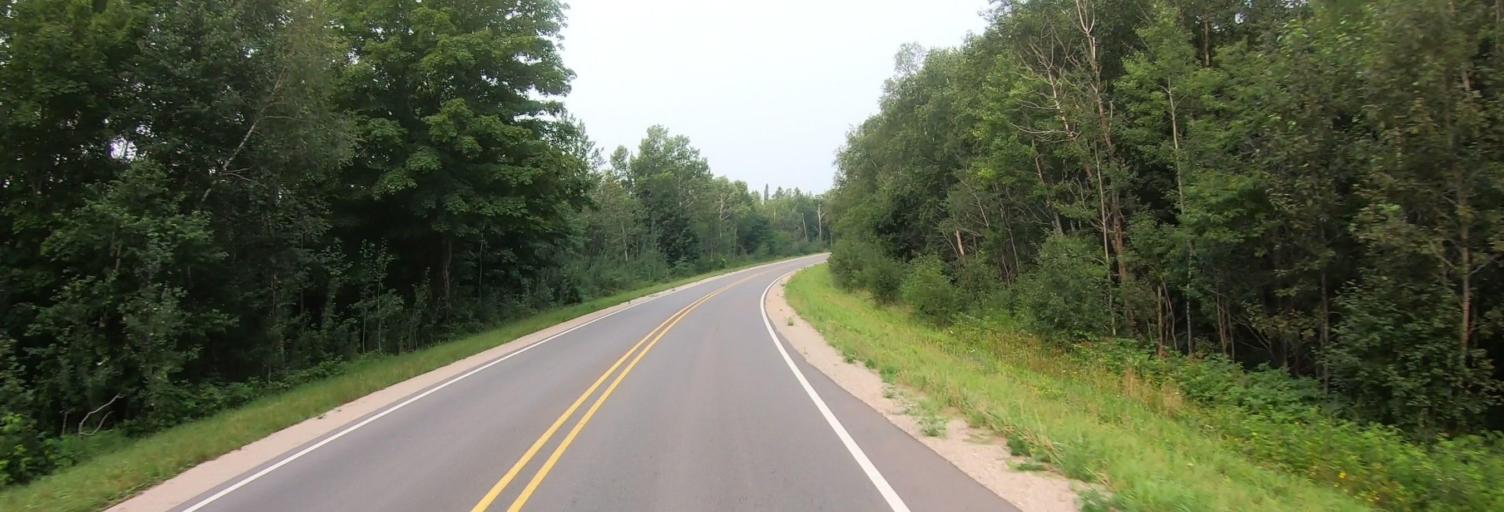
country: US
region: Michigan
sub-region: Luce County
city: Newberry
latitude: 46.4703
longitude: -84.9619
